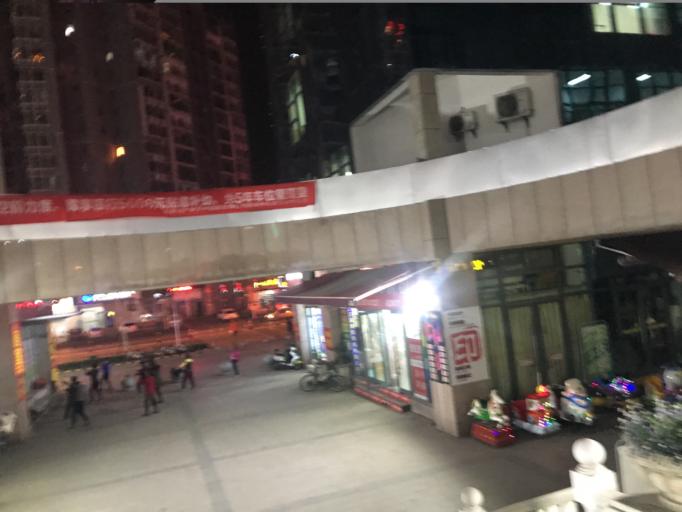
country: CN
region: Hubei
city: Wujia
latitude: 30.6688
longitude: 111.3285
